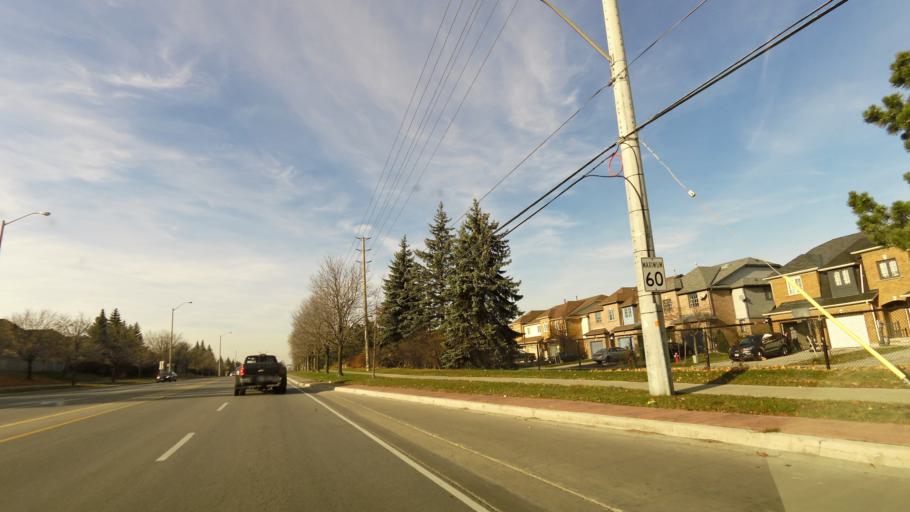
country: CA
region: Ontario
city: Brampton
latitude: 43.7550
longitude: -79.7346
